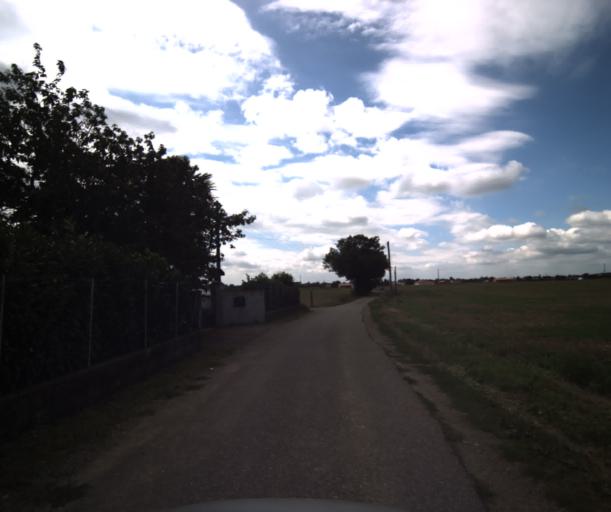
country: FR
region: Midi-Pyrenees
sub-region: Departement de la Haute-Garonne
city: Longages
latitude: 43.3691
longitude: 1.2437
